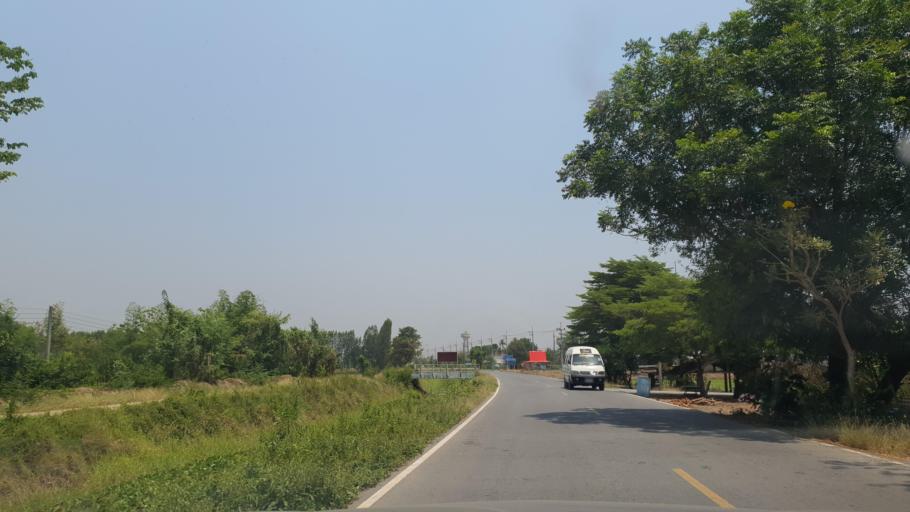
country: TH
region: Suphan Buri
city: Si Prachan
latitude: 14.5808
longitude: 100.1080
